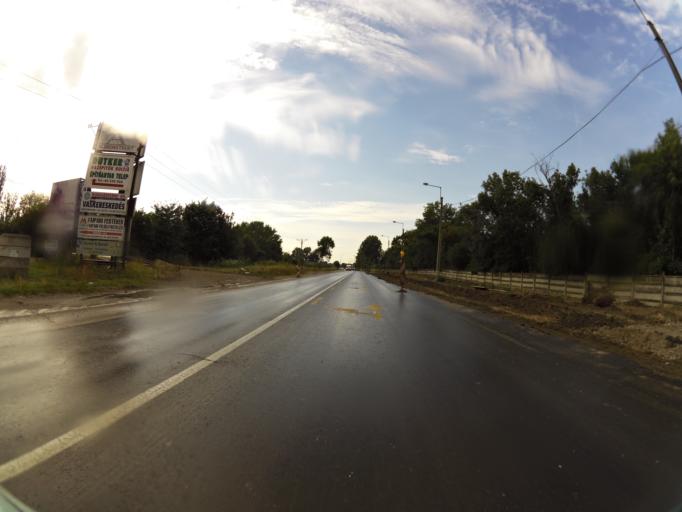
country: HU
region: Csongrad
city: Szeged
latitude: 46.2764
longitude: 20.0986
